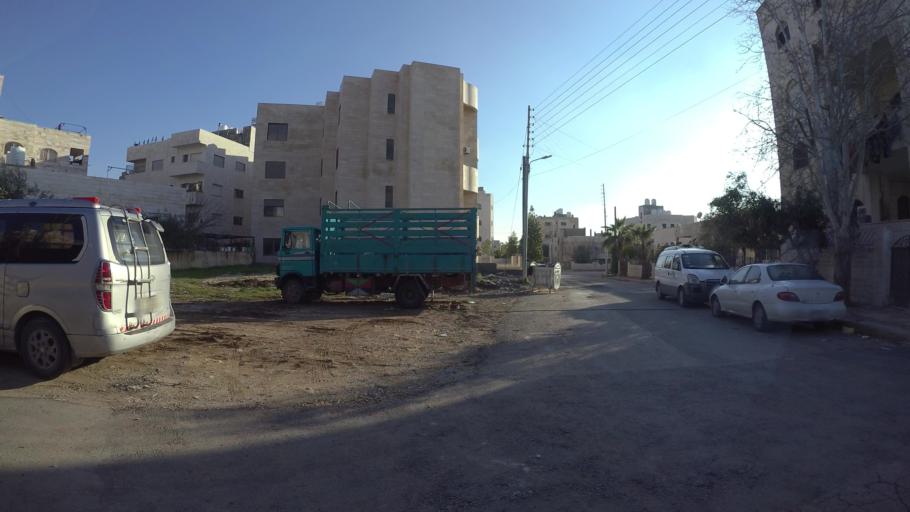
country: JO
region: Amman
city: Al Bunayyat ash Shamaliyah
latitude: 31.8990
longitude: 35.9059
